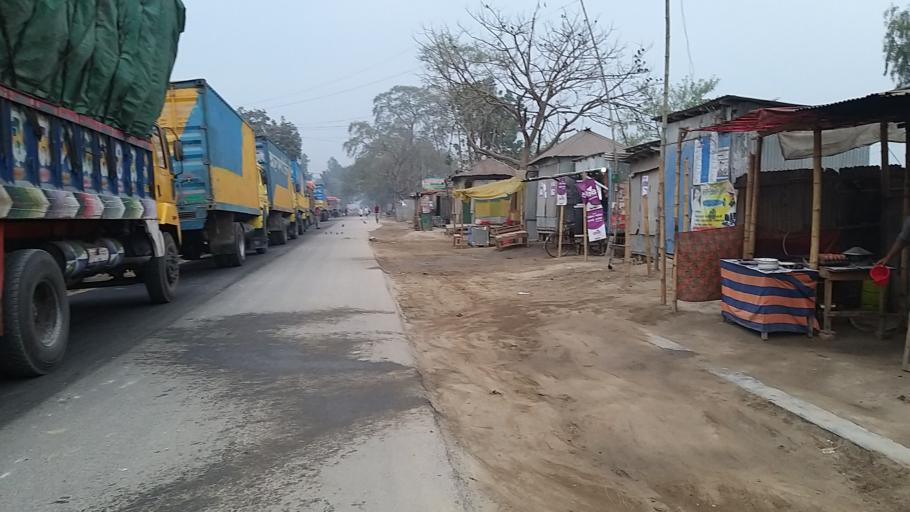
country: IN
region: West Bengal
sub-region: Koch Bihar
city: Haldibari
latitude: 26.4042
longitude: 88.9257
